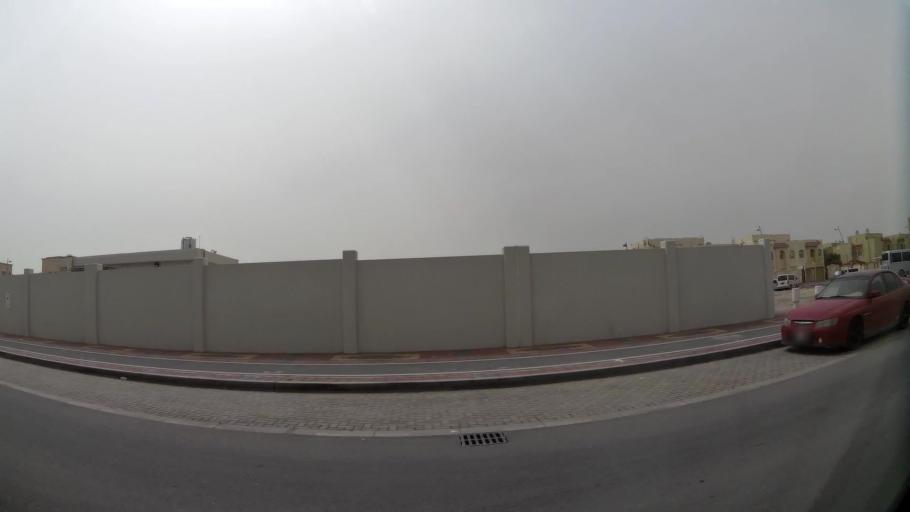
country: QA
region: Baladiyat ad Dawhah
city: Doha
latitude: 25.2368
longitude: 51.5434
